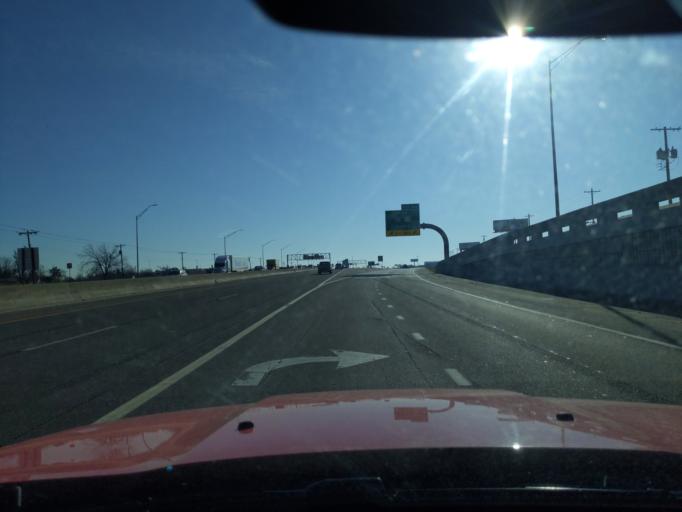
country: US
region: Oklahoma
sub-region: Cleveland County
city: Moore
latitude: 35.3919
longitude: -97.5043
